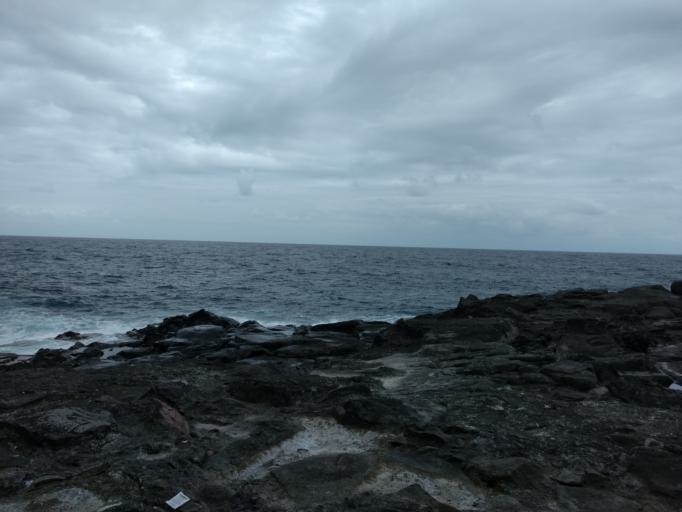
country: PT
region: Madeira
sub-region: Santana
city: Santana
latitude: 32.8373
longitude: -16.9037
